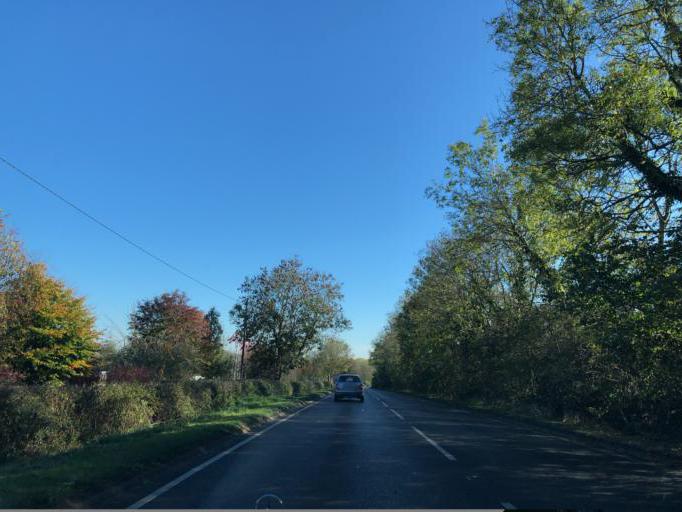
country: GB
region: England
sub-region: Warwickshire
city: Southam
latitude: 52.2534
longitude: -1.4185
